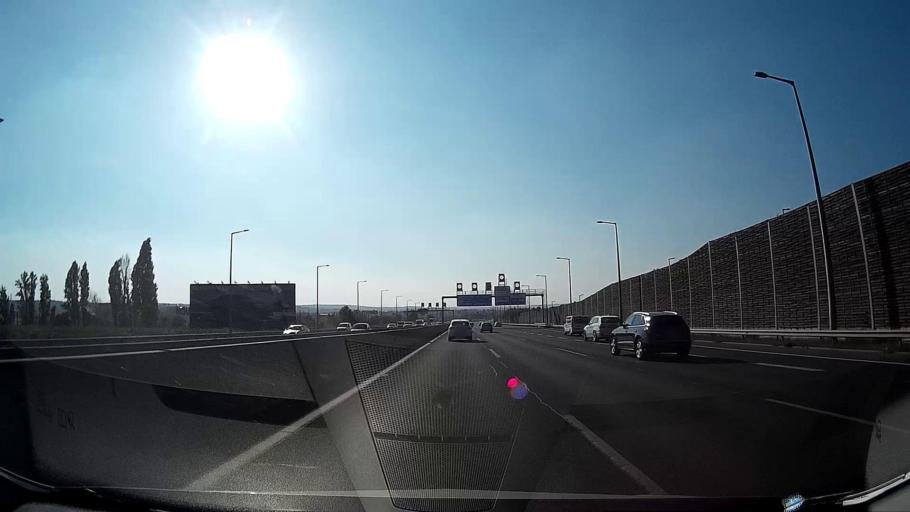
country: HU
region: Pest
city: Budaors
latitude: 47.4560
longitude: 18.9759
